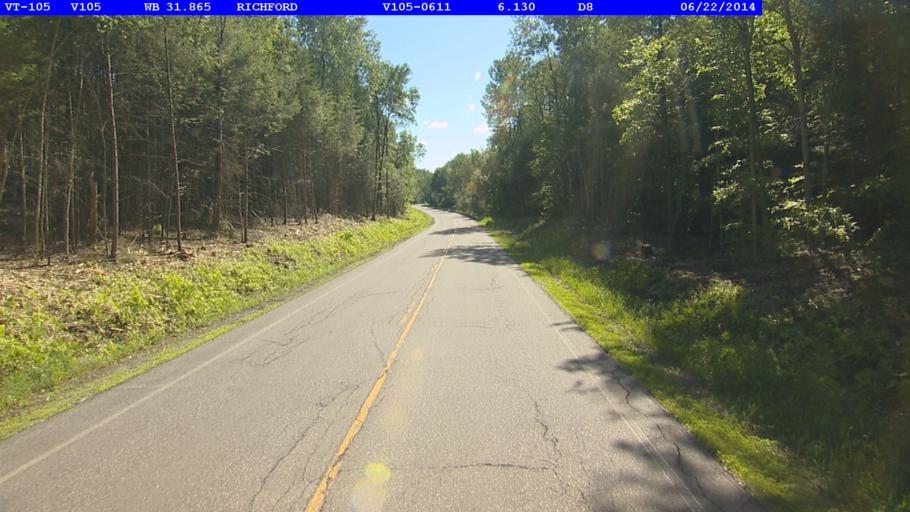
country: US
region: Vermont
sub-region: Franklin County
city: Richford
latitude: 44.9999
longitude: -72.6004
